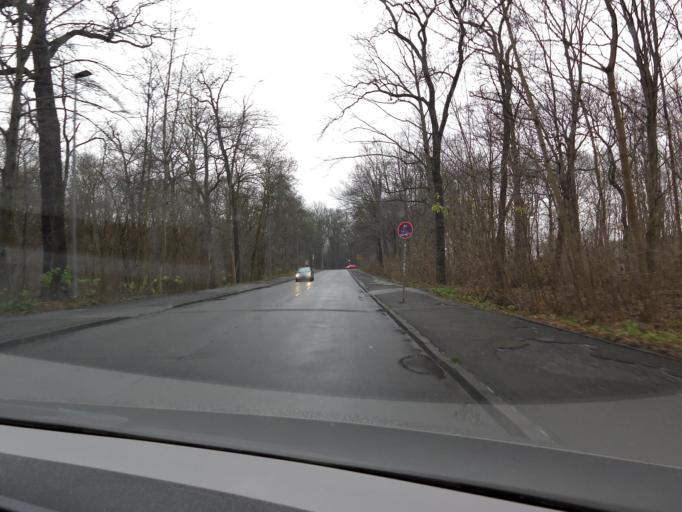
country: DE
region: Saxony
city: Leipzig
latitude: 51.3485
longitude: 12.3397
